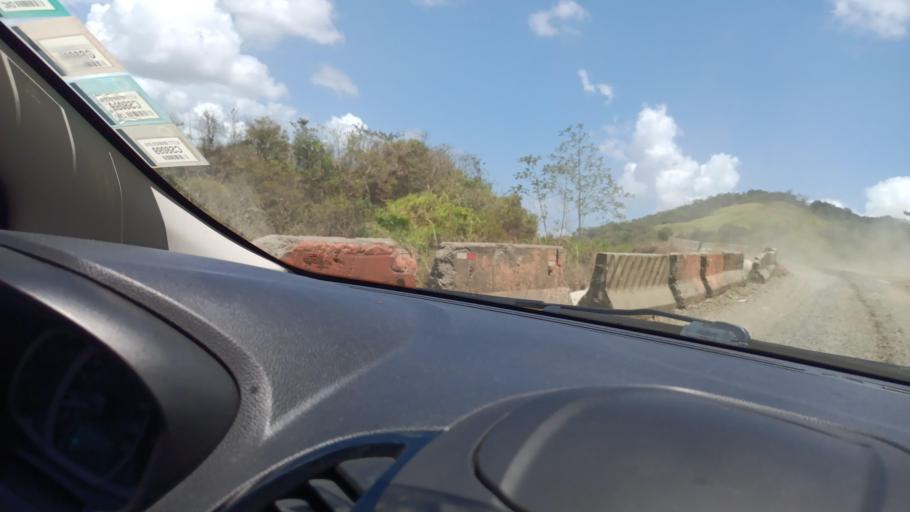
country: PA
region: Panama
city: Alcalde Diaz
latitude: 9.0772
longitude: -79.5737
